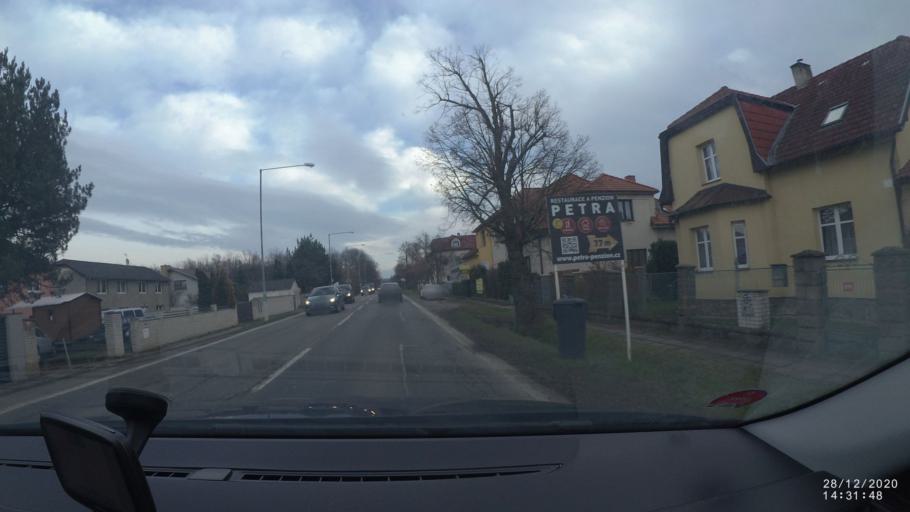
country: CZ
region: Central Bohemia
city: Sestajovice
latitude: 50.0750
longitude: 14.6669
